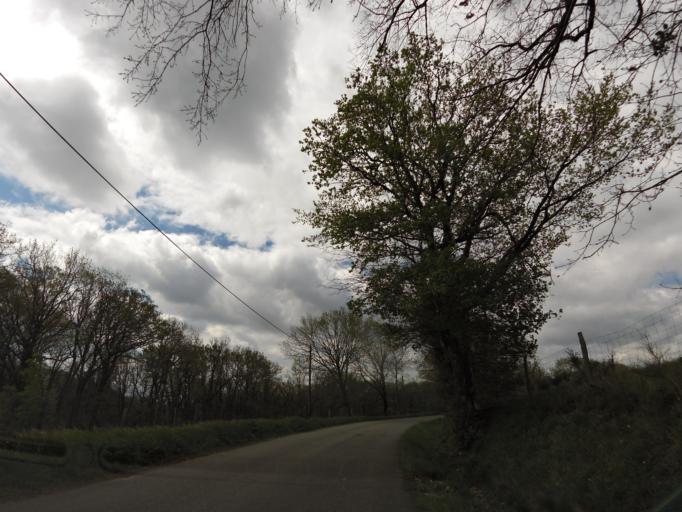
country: FR
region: Languedoc-Roussillon
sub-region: Departement de l'Aude
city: Villepinte
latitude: 43.3557
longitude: 2.1422
